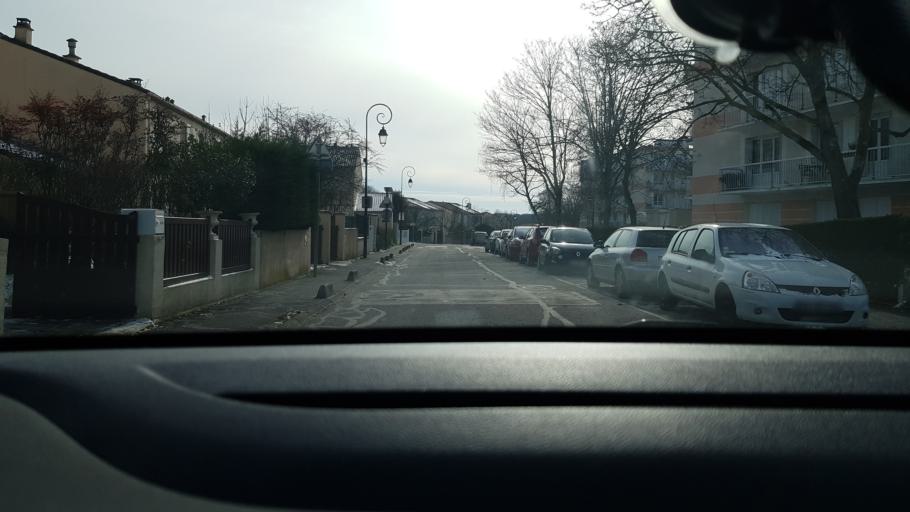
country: FR
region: Ile-de-France
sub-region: Departement de l'Essonne
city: Villiers-le-Bacle
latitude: 48.7177
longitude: 2.1047
